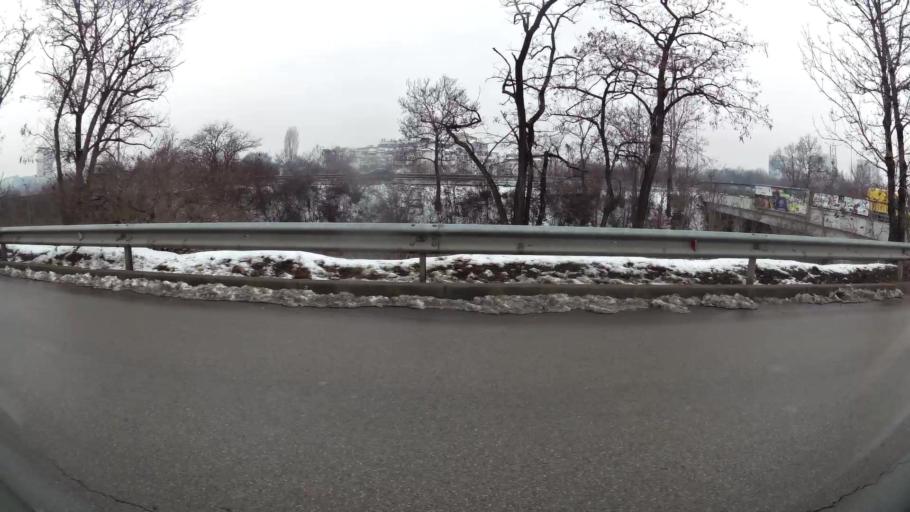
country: BG
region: Sofia-Capital
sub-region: Stolichna Obshtina
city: Sofia
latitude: 42.7201
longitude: 23.3107
